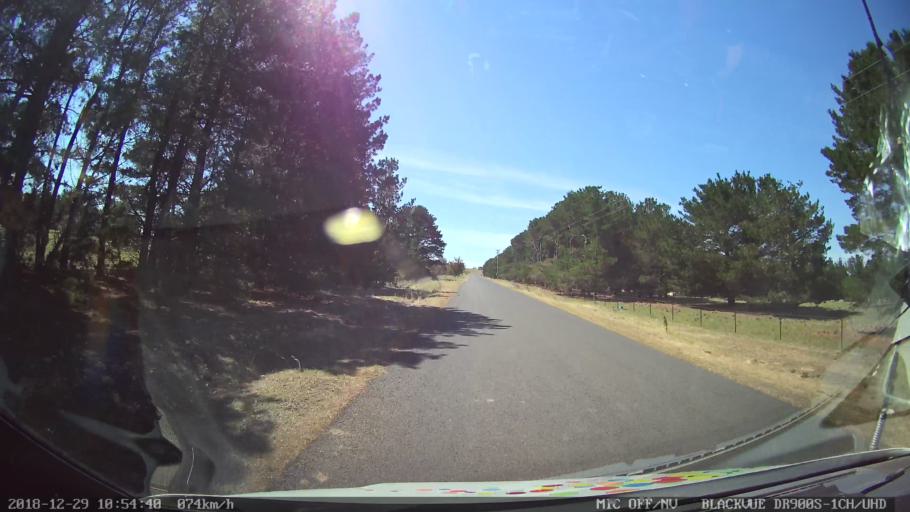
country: AU
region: New South Wales
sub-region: Palerang
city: Bungendore
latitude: -35.1167
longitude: 149.5285
